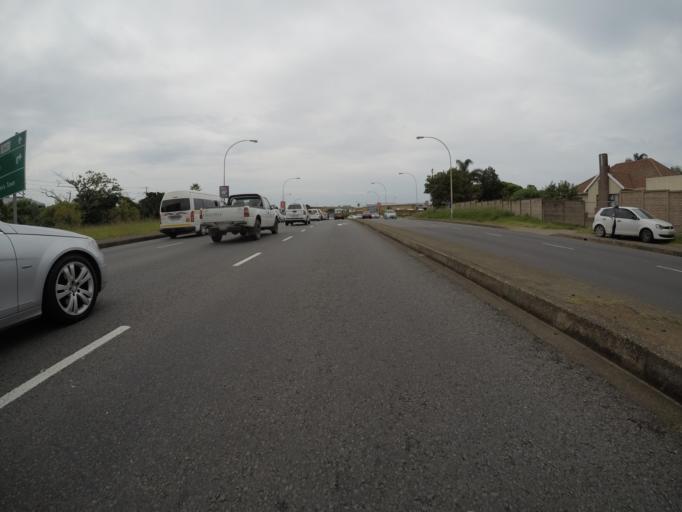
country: ZA
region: Eastern Cape
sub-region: Buffalo City Metropolitan Municipality
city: East London
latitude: -32.9850
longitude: 27.8967
